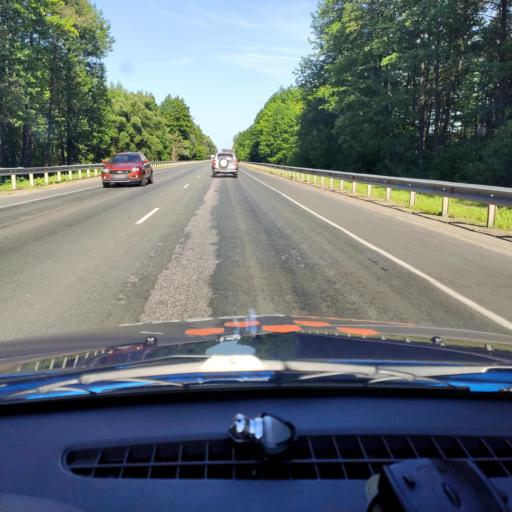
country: RU
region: Voronezj
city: Orlovo
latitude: 51.6816
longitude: 39.5775
